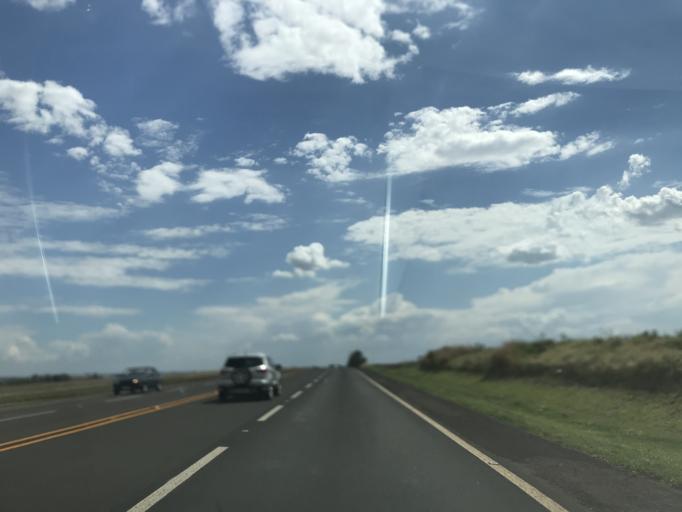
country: BR
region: Parana
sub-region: Arapongas
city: Arapongas
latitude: -23.4243
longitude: -51.5226
